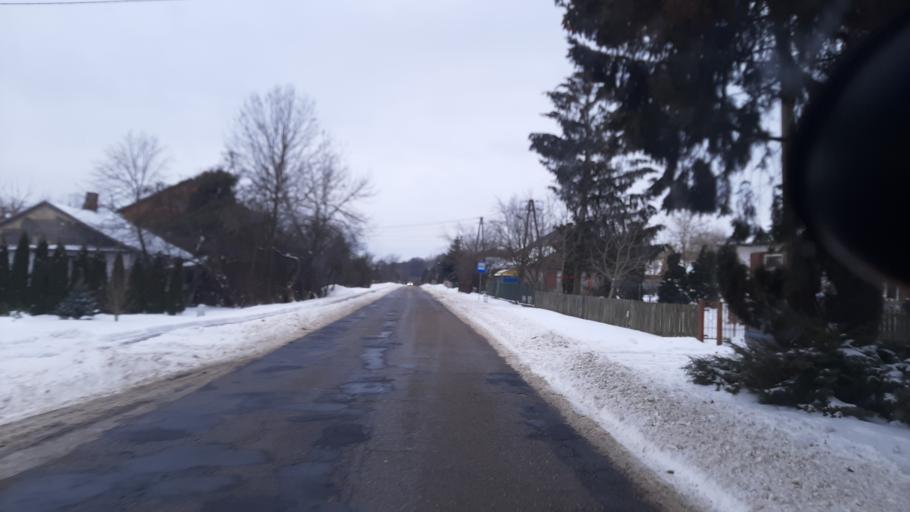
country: PL
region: Lublin Voivodeship
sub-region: Powiat pulawski
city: Kurow
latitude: 51.4336
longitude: 22.2271
